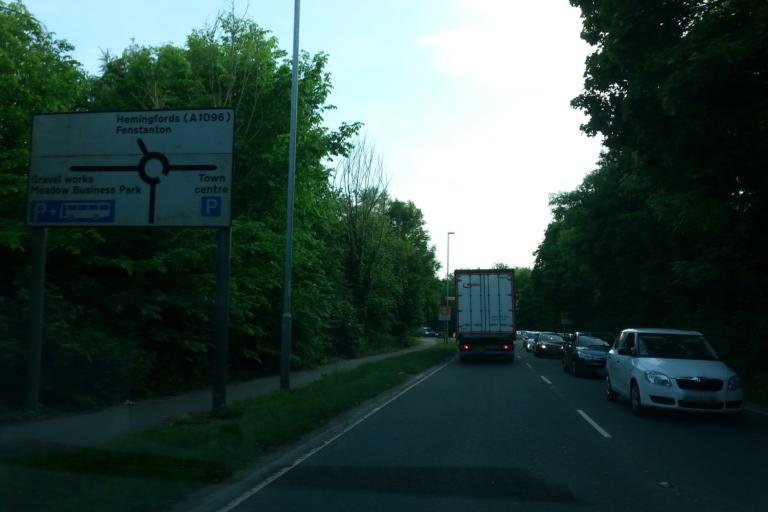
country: GB
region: England
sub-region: Cambridgeshire
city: Hemingford Grey
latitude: 52.3249
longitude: -0.0680
